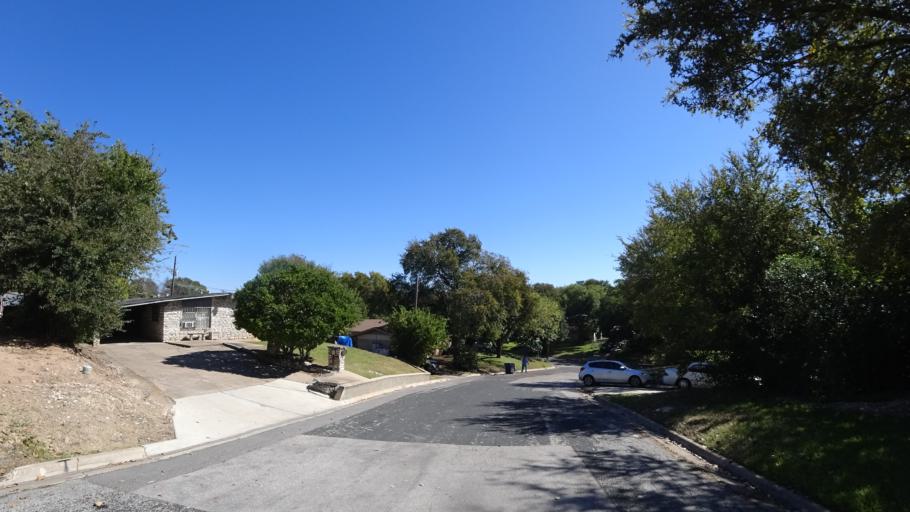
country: US
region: Texas
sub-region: Travis County
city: Austin
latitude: 30.2856
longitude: -97.6796
